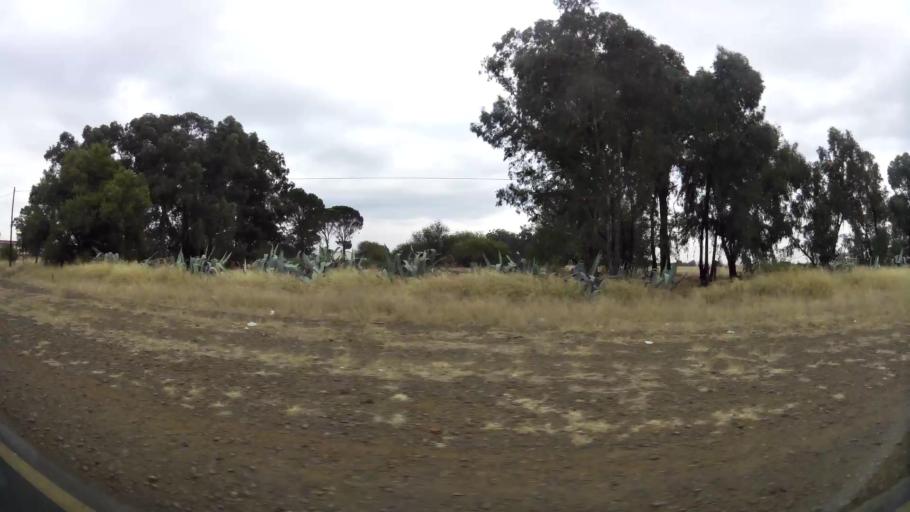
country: ZA
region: Orange Free State
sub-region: Fezile Dabi District Municipality
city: Kroonstad
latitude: -27.6200
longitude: 27.2336
